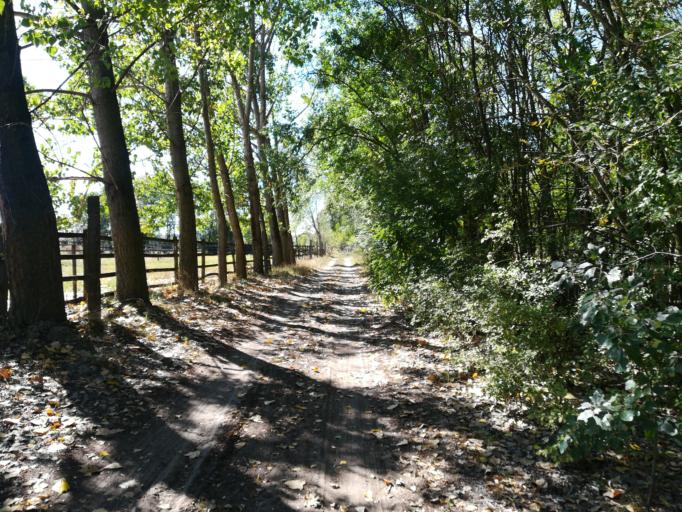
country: HU
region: Bacs-Kiskun
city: Tiszakecske
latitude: 46.9477
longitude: 20.0784
